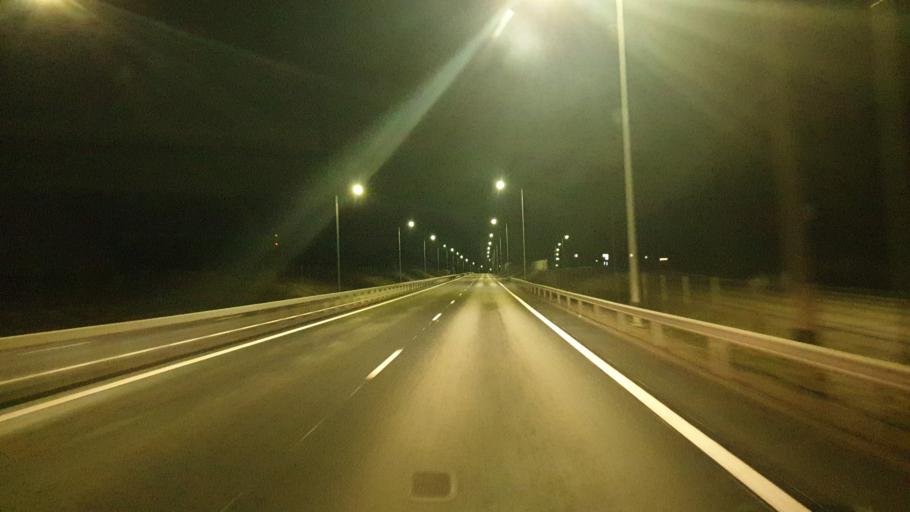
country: FI
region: Central Finland
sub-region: AEaenekoski
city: AEaenekoski
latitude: 62.5922
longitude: 25.6933
